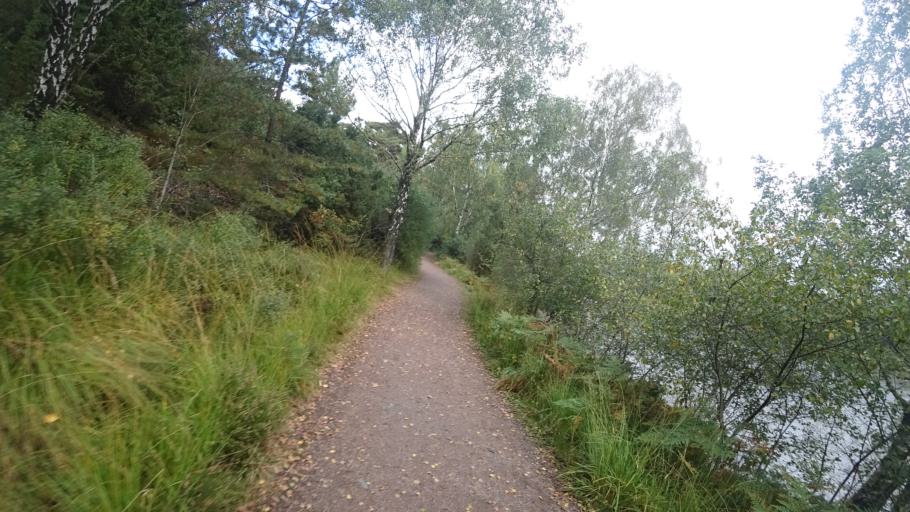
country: SE
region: Vaestra Goetaland
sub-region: Goteborg
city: Billdal
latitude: 57.6073
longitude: 11.9696
